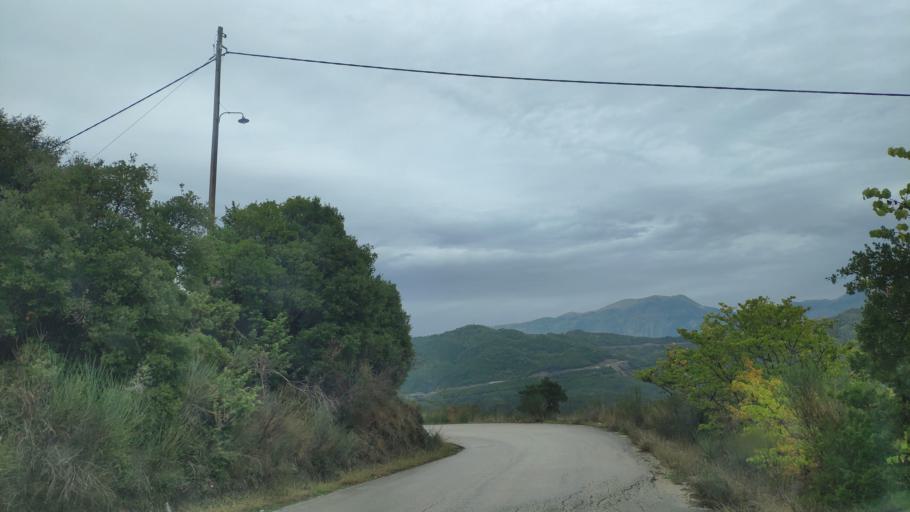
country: GR
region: Epirus
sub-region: Nomos Thesprotias
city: Paramythia
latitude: 39.4638
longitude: 20.6722
